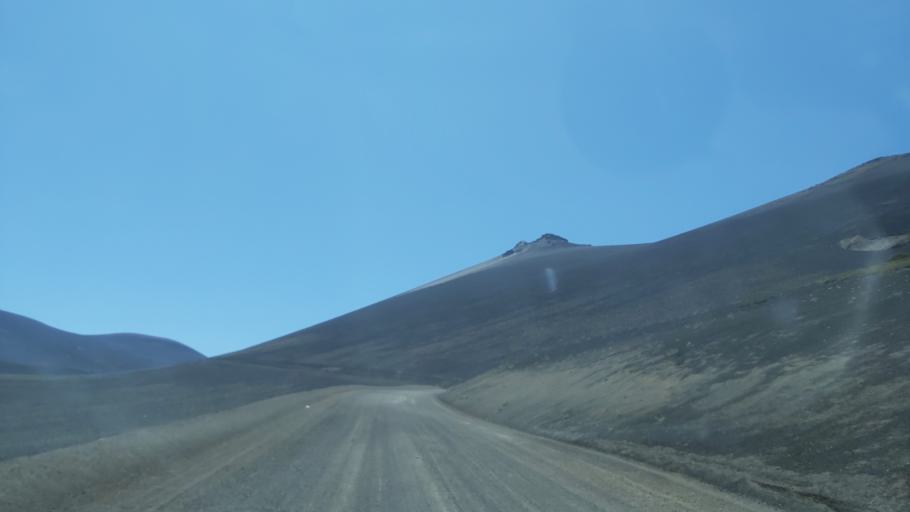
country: CL
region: Araucania
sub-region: Provincia de Cautin
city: Vilcun
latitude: -38.4104
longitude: -71.5422
